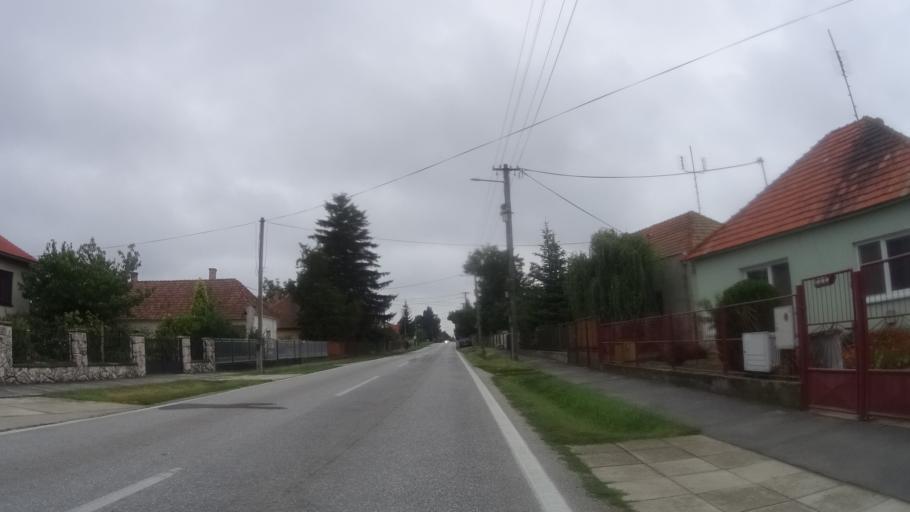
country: HU
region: Komarom-Esztergom
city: Neszmely
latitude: 47.7460
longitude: 18.3624
